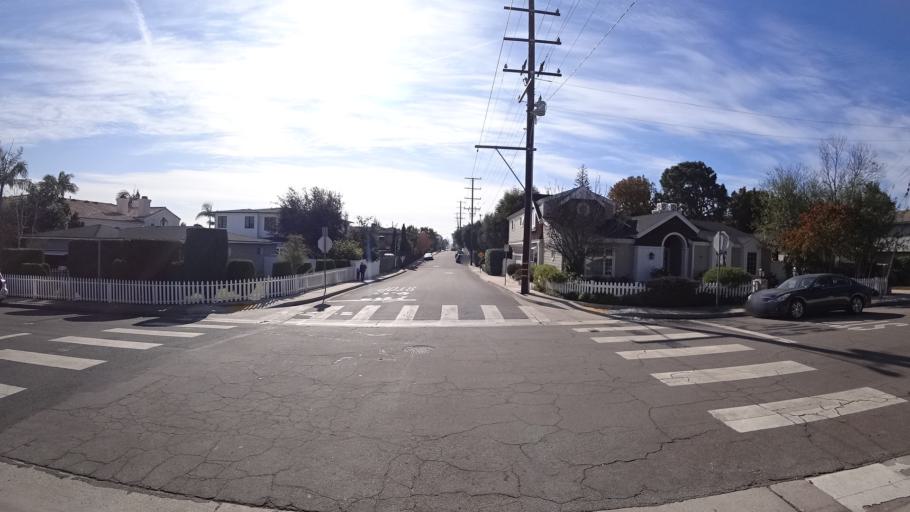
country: US
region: California
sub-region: Los Angeles County
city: Manhattan Beach
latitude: 33.8856
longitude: -118.3874
